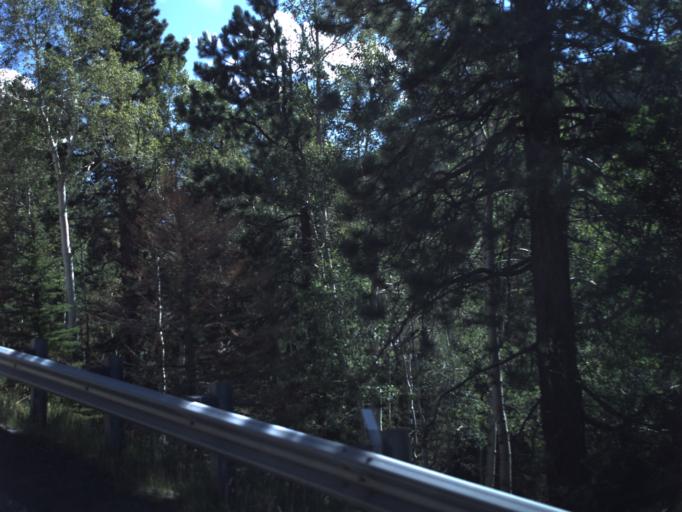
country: US
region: Utah
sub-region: Piute County
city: Junction
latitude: 38.3137
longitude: -112.3946
